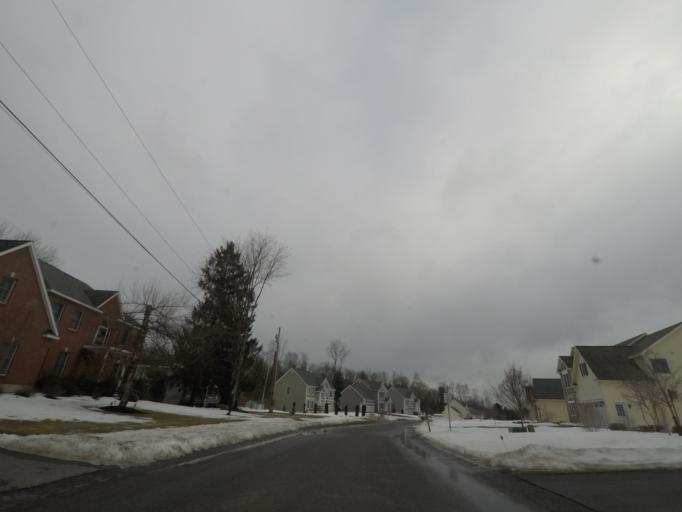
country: US
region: New York
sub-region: Schenectady County
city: Rotterdam
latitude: 42.7672
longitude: -73.9783
